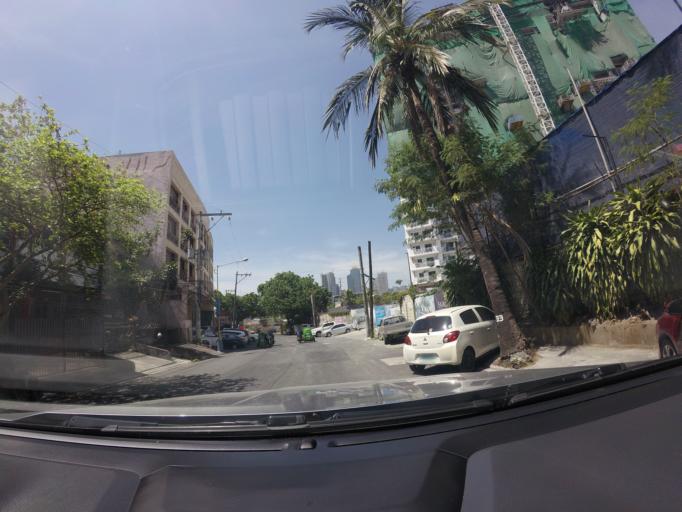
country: PH
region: Metro Manila
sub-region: Pasig
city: Pasig City
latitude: 14.5694
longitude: 121.0557
